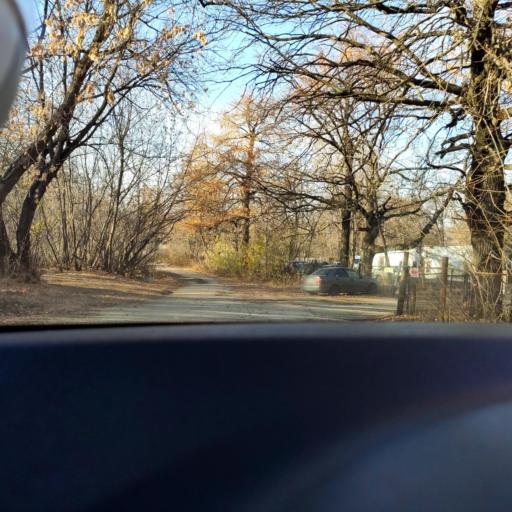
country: RU
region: Samara
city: Samara
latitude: 53.2238
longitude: 50.1638
